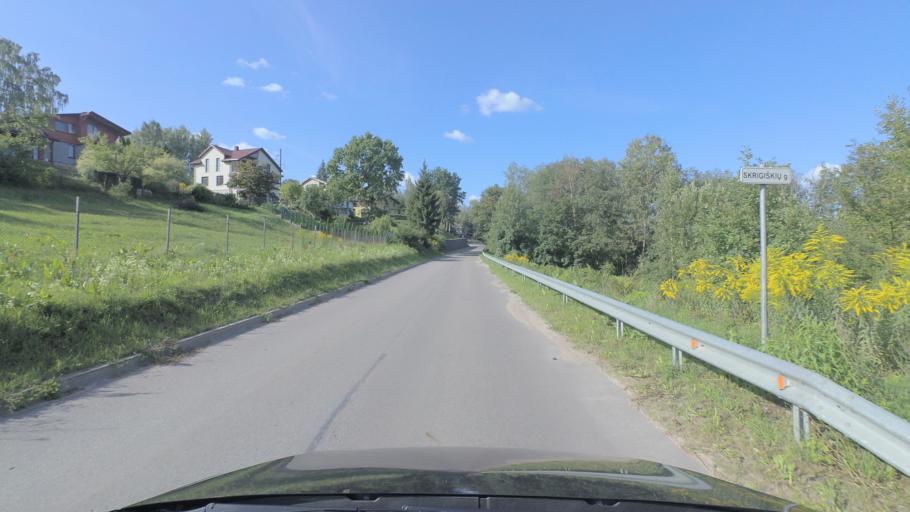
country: LT
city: Nemencine
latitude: 54.8485
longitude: 25.3736
